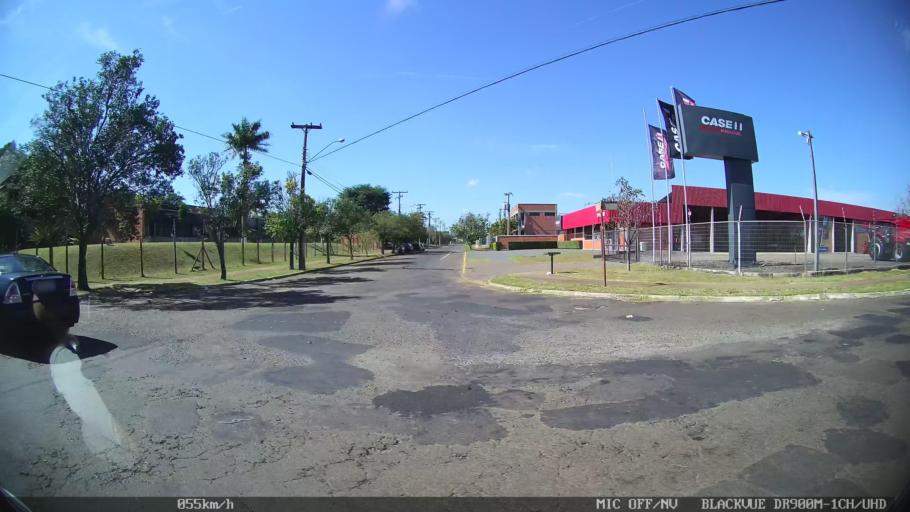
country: BR
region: Sao Paulo
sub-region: Franca
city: Franca
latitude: -20.5509
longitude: -47.4370
